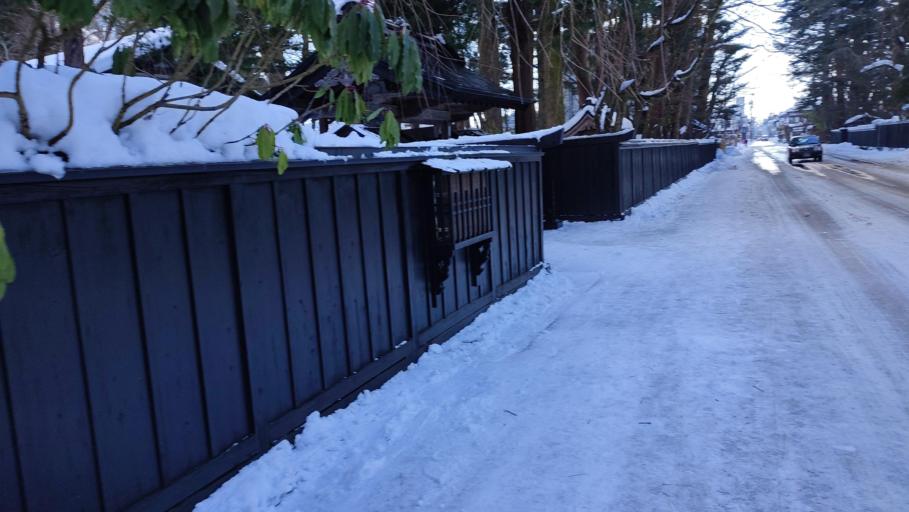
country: JP
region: Akita
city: Kakunodatemachi
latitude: 39.5973
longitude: 140.5622
